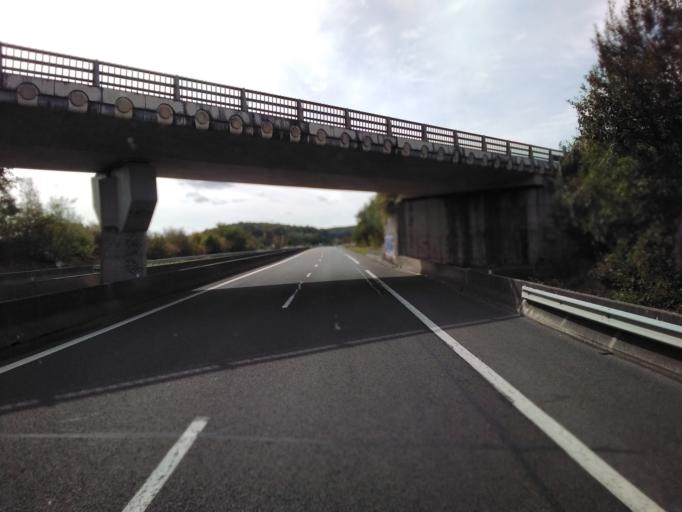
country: FR
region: Champagne-Ardenne
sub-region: Departement des Ardennes
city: Attigny
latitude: 49.6260
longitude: 4.5531
